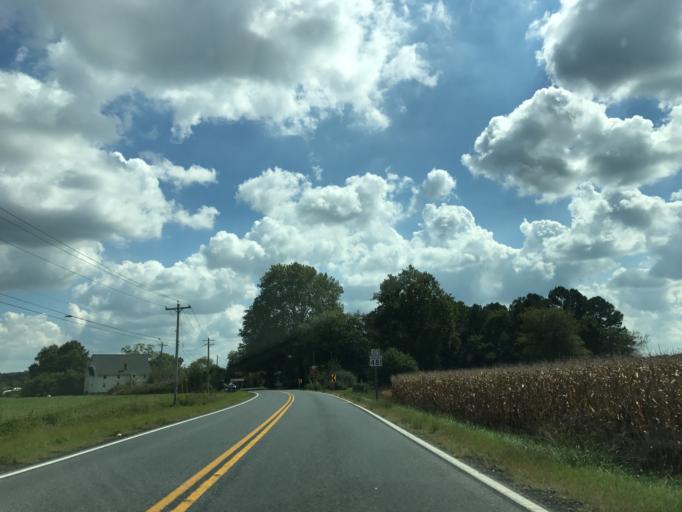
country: US
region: Maryland
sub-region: Caroline County
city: Ridgely
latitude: 39.0041
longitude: -75.9614
